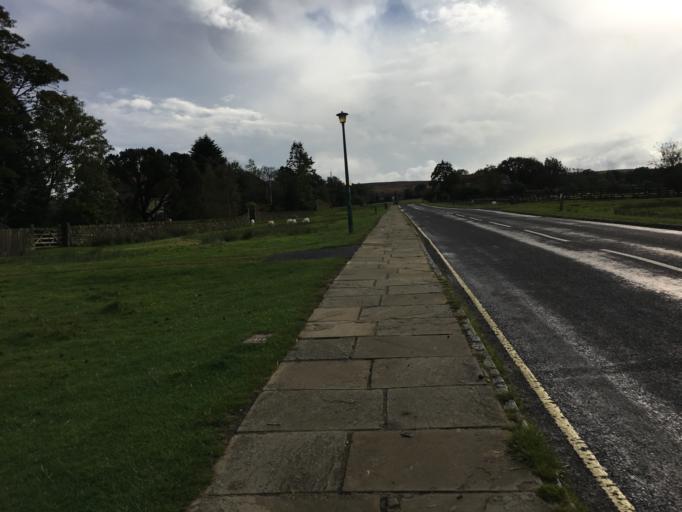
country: GB
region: England
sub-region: North Yorkshire
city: Sleights
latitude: 54.3989
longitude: -0.7216
